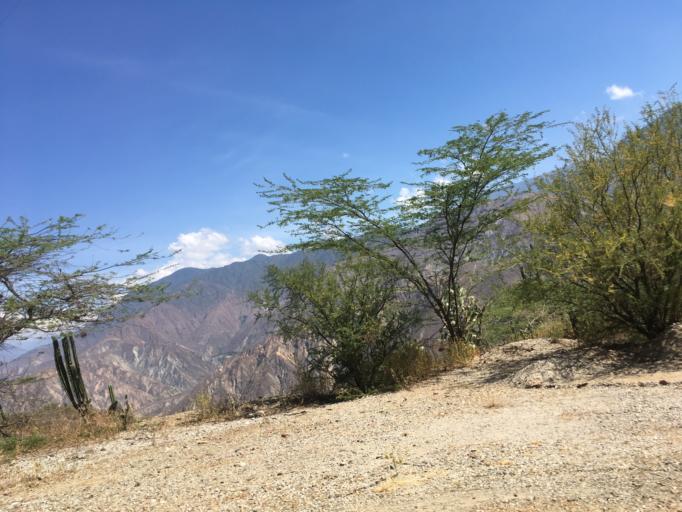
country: CO
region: Santander
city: Aratoca
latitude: 6.7772
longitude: -72.9936
